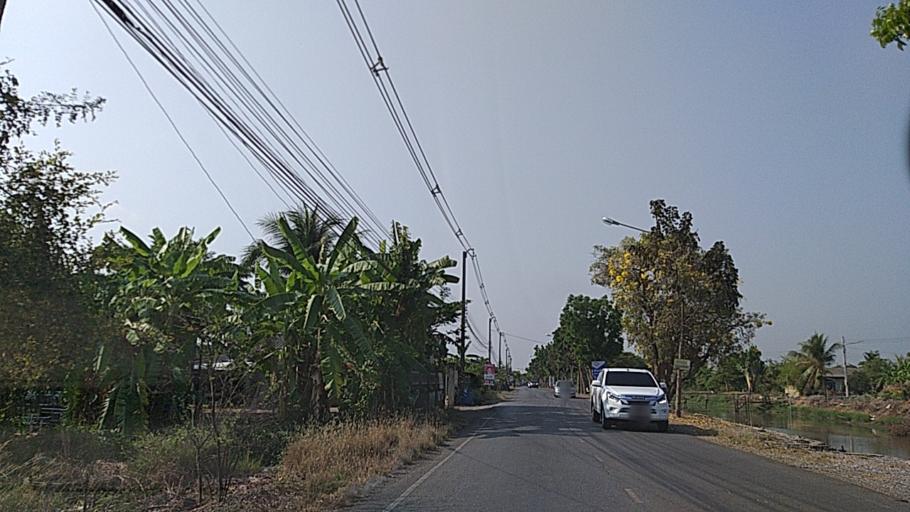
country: TH
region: Pathum Thani
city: Lam Luk Ka
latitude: 13.9672
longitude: 100.7063
